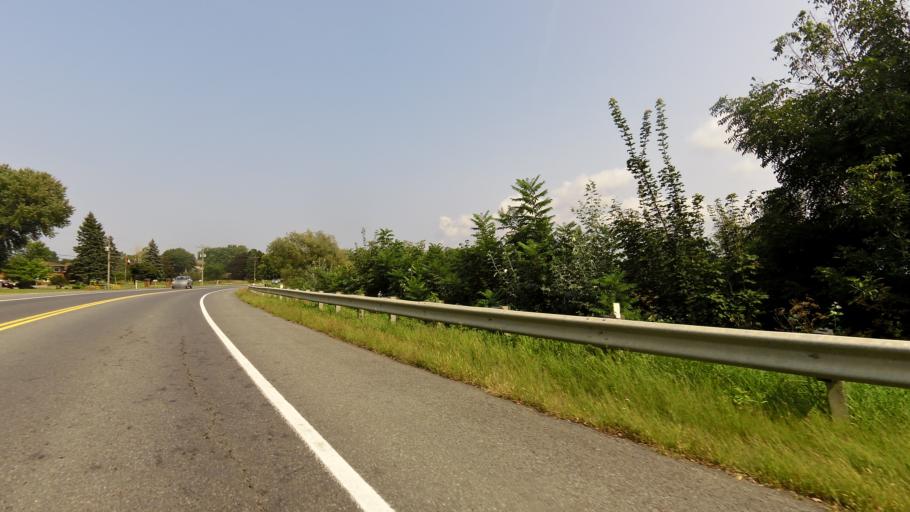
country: CA
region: Ontario
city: Prescott
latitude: 44.7025
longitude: -75.5278
